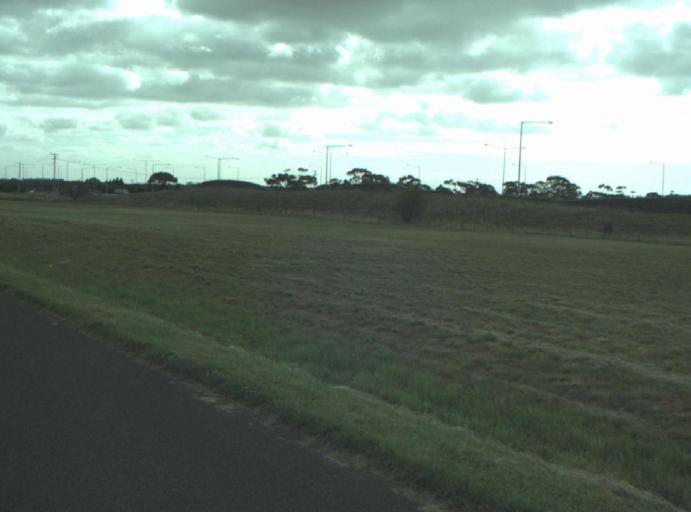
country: AU
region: Victoria
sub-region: Greater Geelong
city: Lara
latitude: -38.0541
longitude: 144.3924
